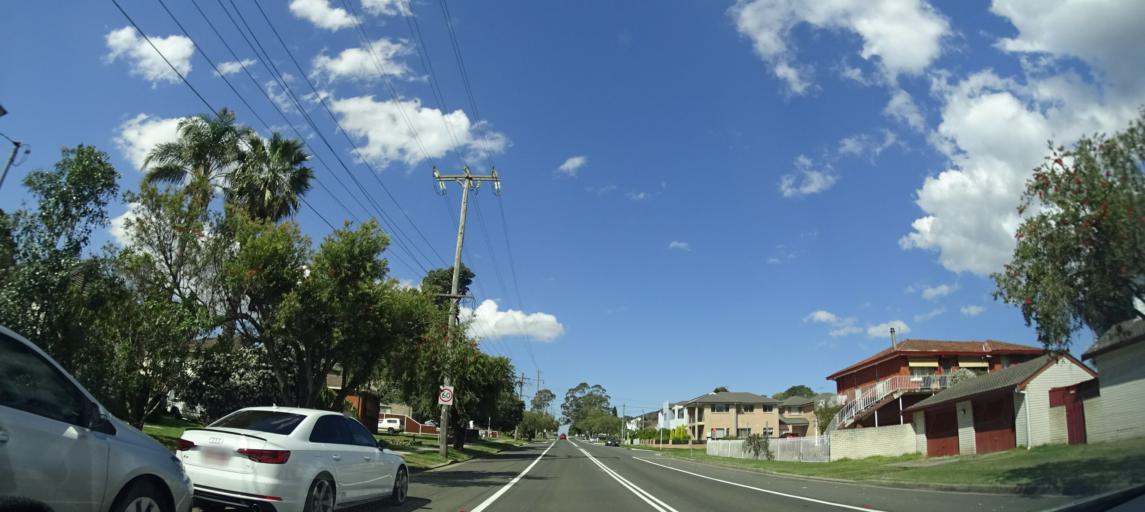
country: AU
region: New South Wales
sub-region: Bankstown
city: Revesby
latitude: -33.9464
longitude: 151.0031
